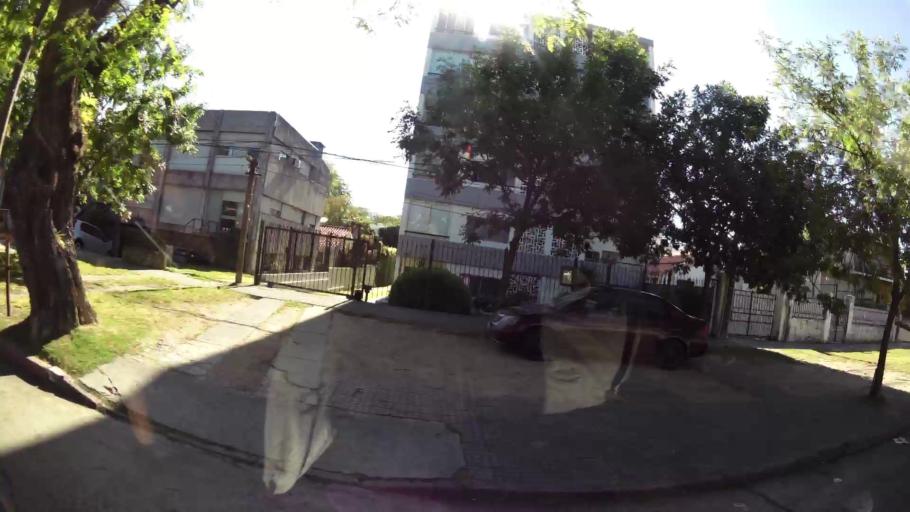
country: UY
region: Canelones
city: Paso de Carrasco
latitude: -34.8903
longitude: -56.0801
